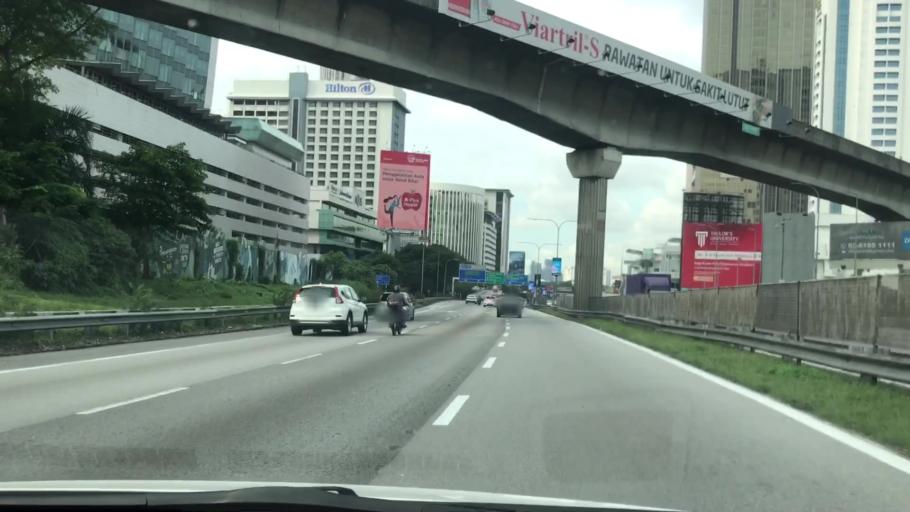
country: MY
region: Selangor
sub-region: Petaling
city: Petaling Jaya
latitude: 3.1047
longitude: 101.6431
